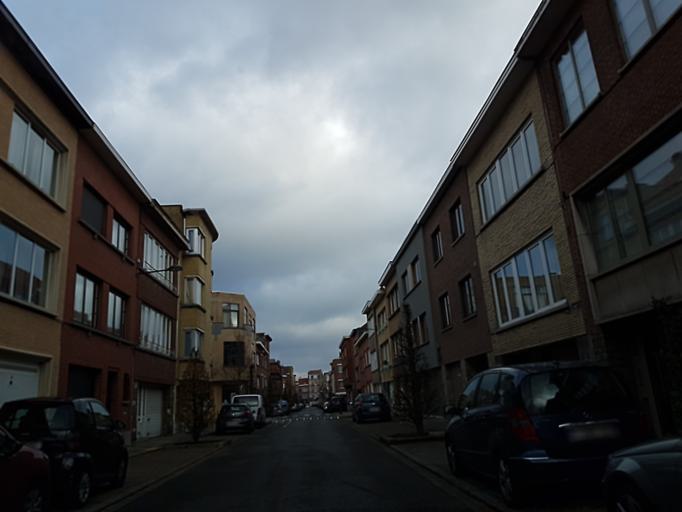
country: BE
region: Flanders
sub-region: Provincie Vlaams-Brabant
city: Diegem
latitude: 50.8697
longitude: 4.3964
